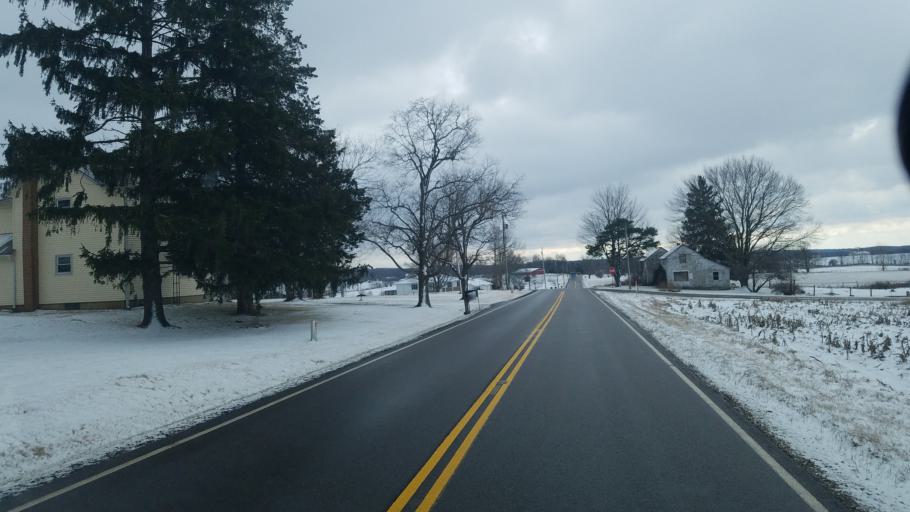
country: US
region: Ohio
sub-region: Knox County
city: Fredericktown
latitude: 40.5320
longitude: -82.5571
